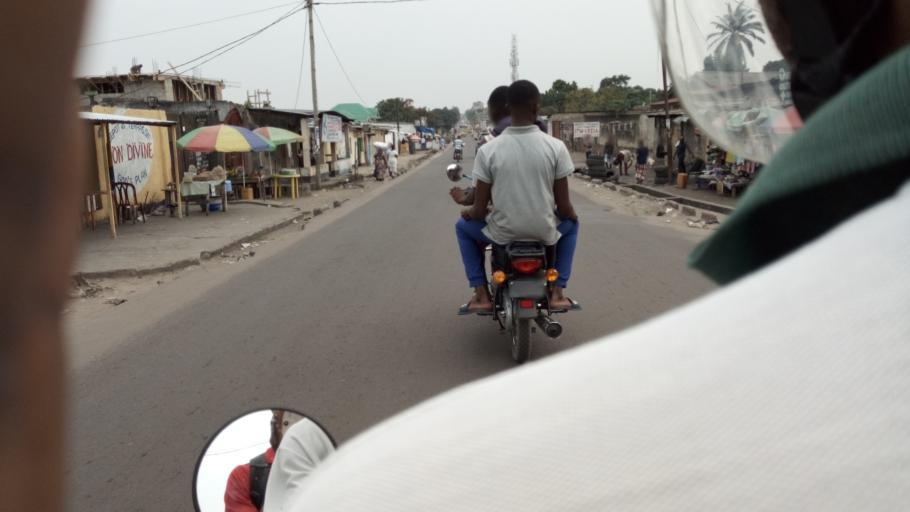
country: CD
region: Kinshasa
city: Masina
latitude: -4.4097
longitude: 15.3163
